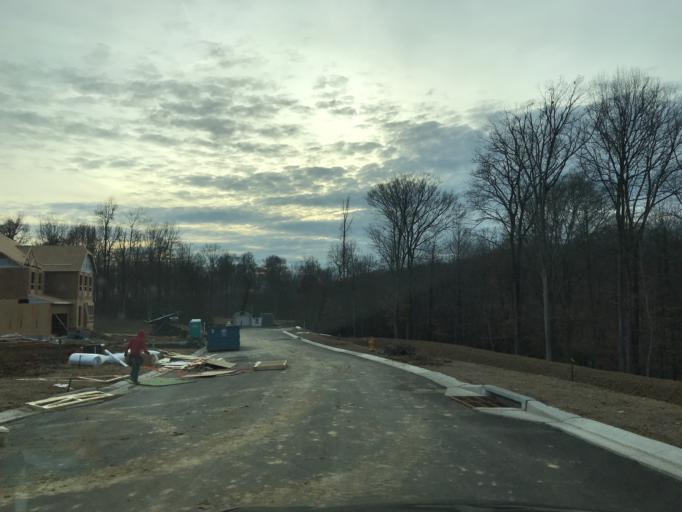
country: US
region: Maryland
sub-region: Harford County
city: Bel Air
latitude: 39.5098
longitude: -76.3506
